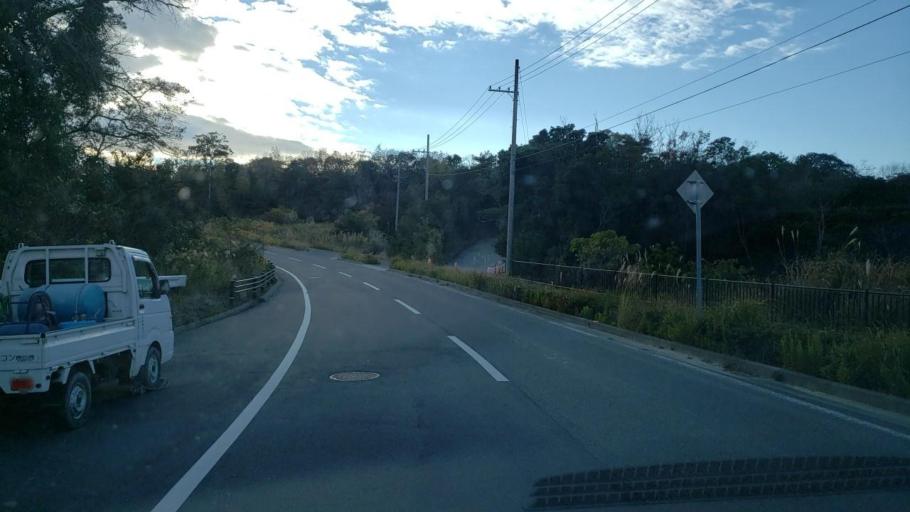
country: JP
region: Hyogo
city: Akashi
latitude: 34.5792
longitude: 134.9850
